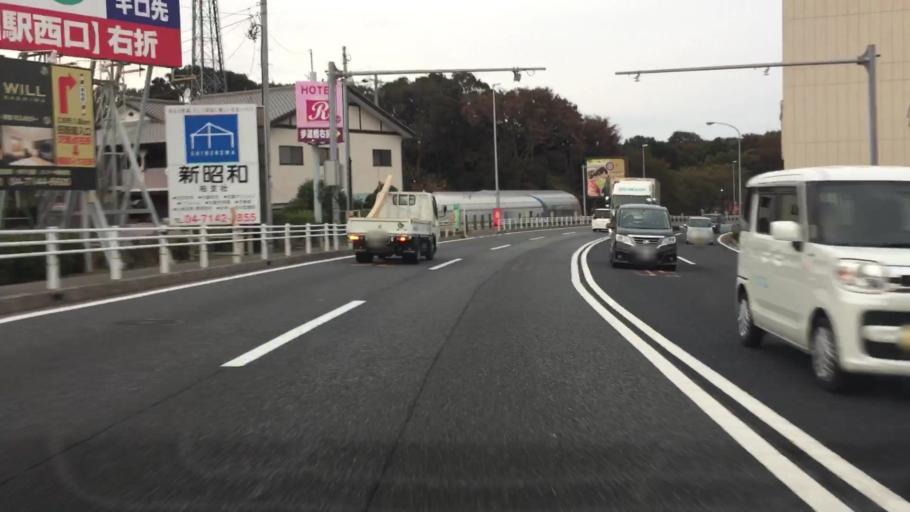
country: JP
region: Chiba
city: Kashiwa
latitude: 35.8389
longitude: 139.9402
